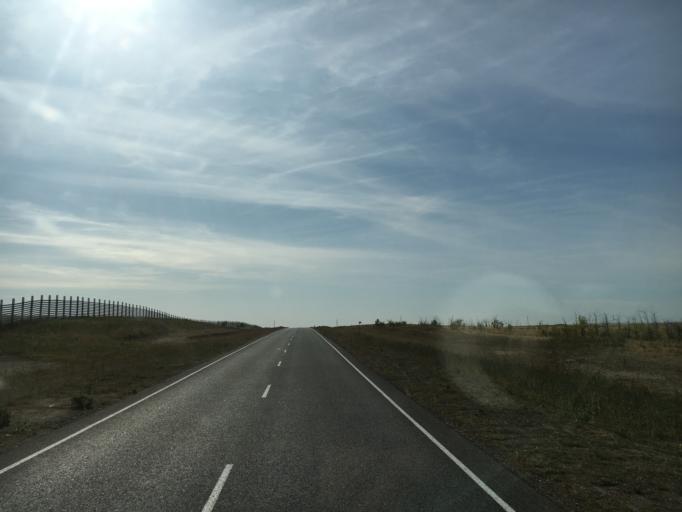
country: KZ
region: Batys Qazaqstan
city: Kamenka
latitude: 51.1090
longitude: 50.4475
